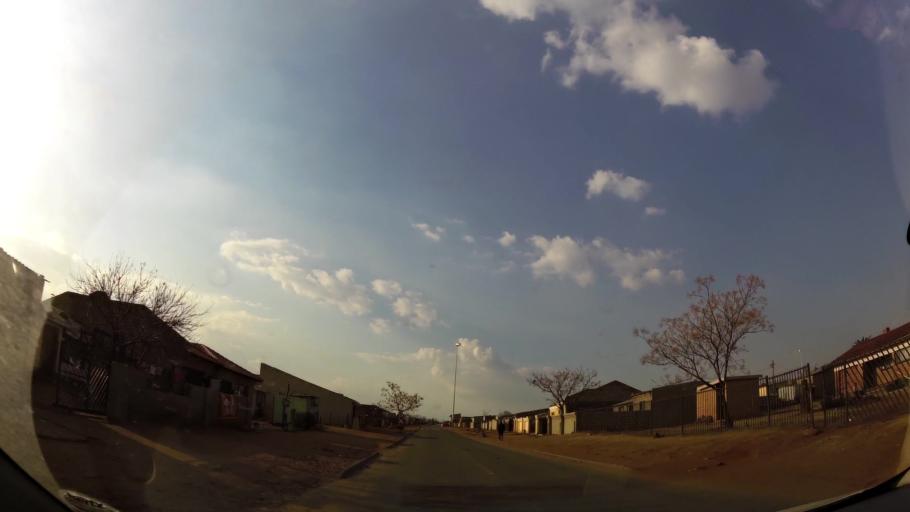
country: ZA
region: Gauteng
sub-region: Ekurhuleni Metropolitan Municipality
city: Germiston
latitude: -26.3493
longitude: 28.2084
